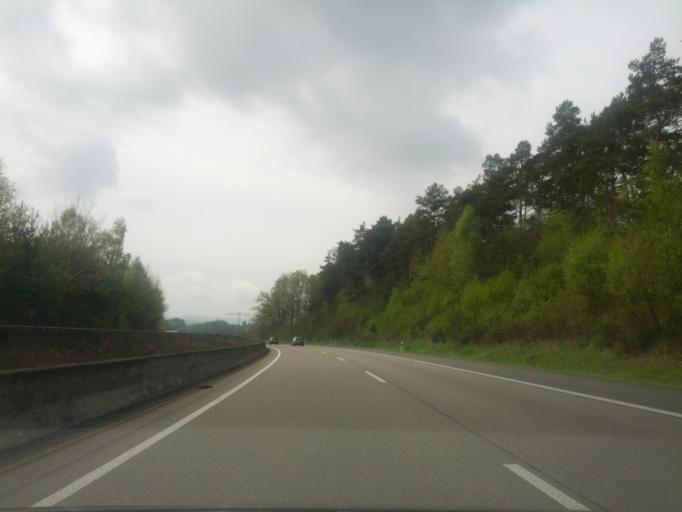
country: DE
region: Thuringia
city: Gerstungen
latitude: 50.9837
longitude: 10.0715
